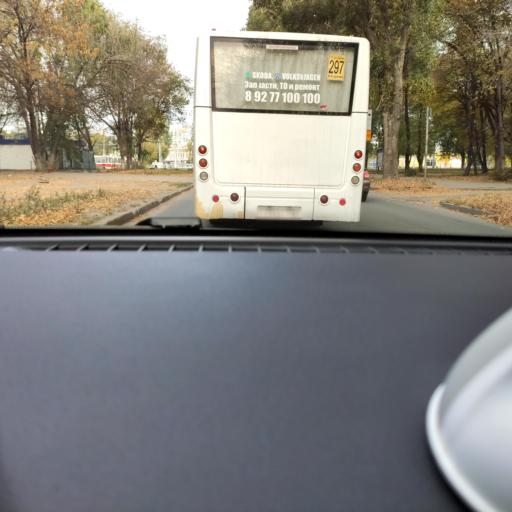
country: RU
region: Samara
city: Samara
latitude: 53.2481
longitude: 50.2489
